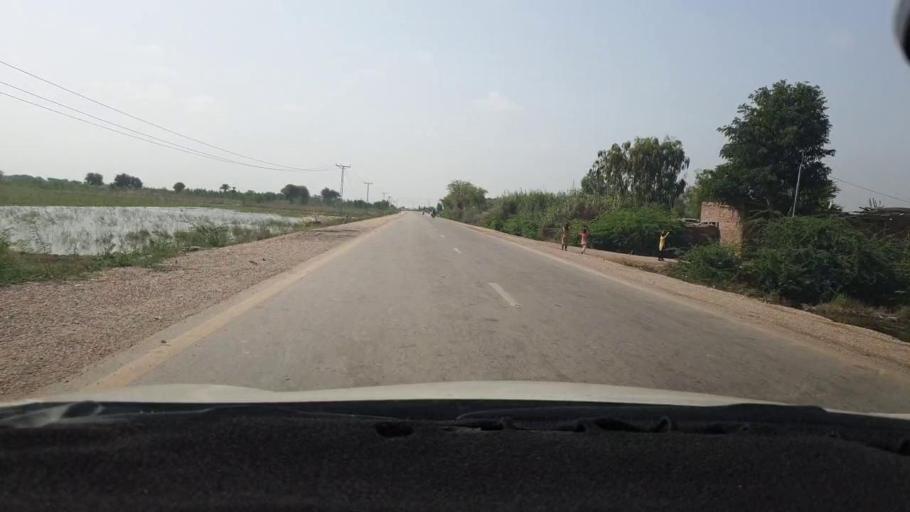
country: PK
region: Sindh
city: Tando Mittha Khan
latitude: 25.7905
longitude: 69.0713
